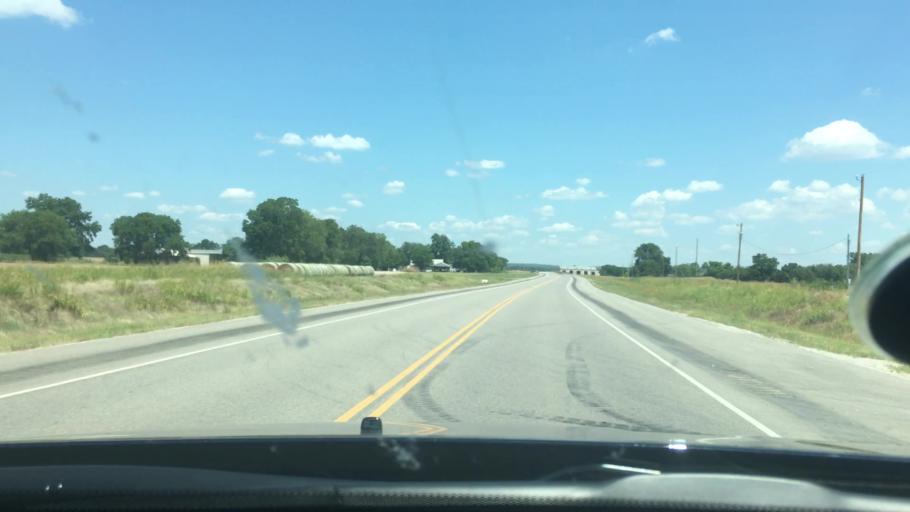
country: US
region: Oklahoma
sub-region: Carter County
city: Dickson
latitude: 34.2289
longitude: -96.9768
